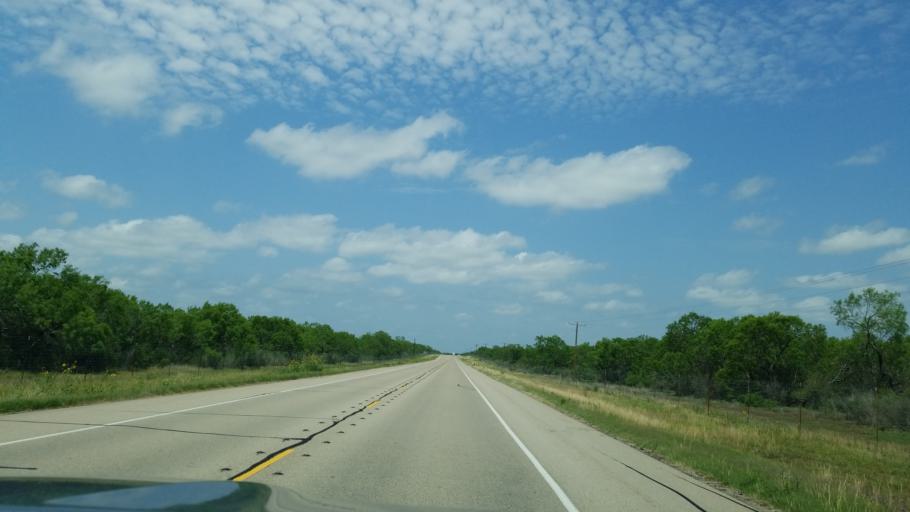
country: US
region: Texas
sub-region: Frio County
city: Pearsall
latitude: 29.0078
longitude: -99.1908
